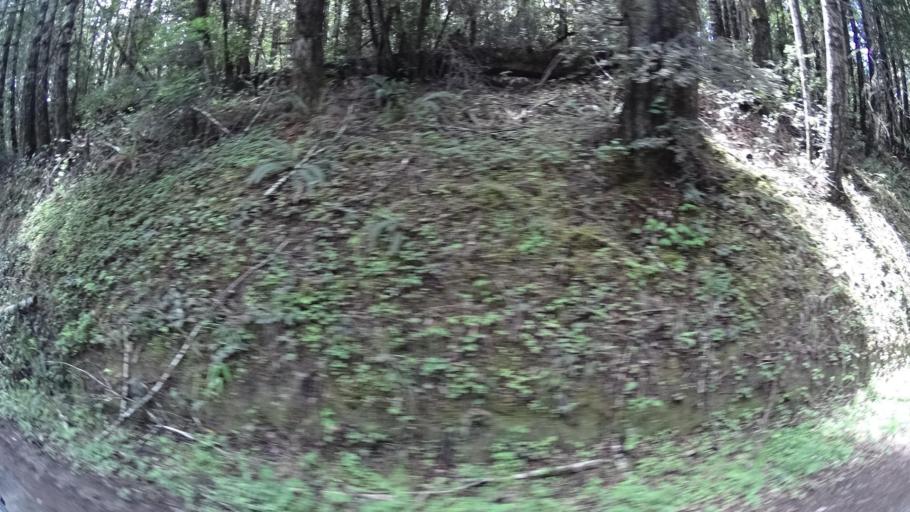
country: US
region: California
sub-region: Humboldt County
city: Blue Lake
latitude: 40.7988
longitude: -123.8753
